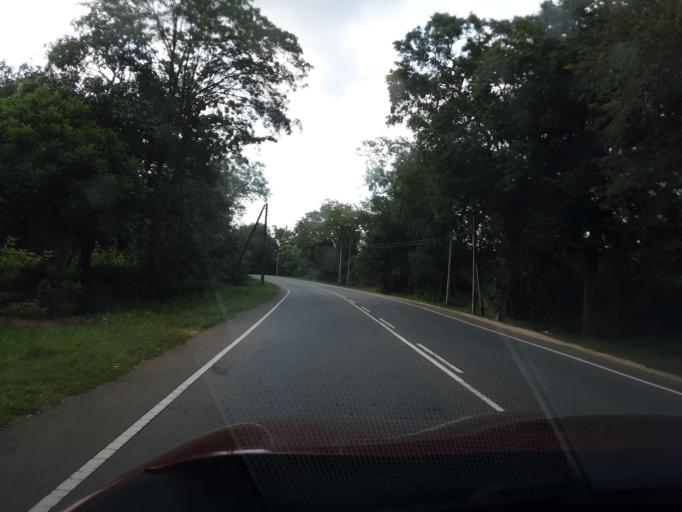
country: LK
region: Uva
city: Haputale
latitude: 6.3698
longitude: 81.1727
